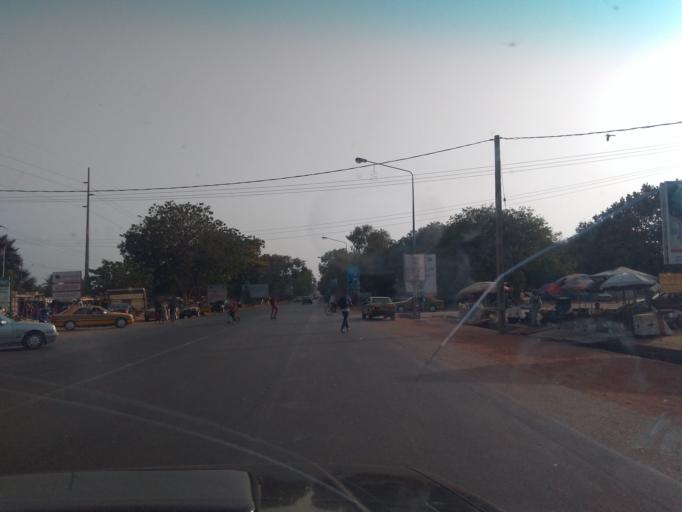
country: GM
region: Banjul
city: Bakau
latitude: 13.4639
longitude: -16.6893
